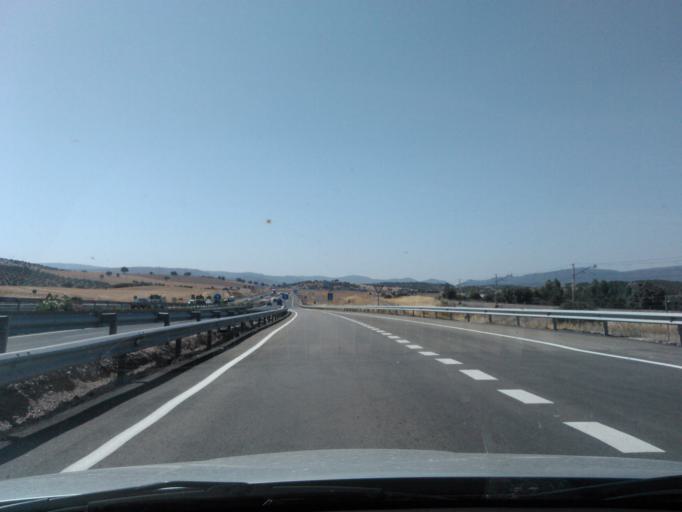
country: ES
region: Castille-La Mancha
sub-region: Provincia de Ciudad Real
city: Viso del Marques
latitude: 38.4949
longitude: -3.5034
